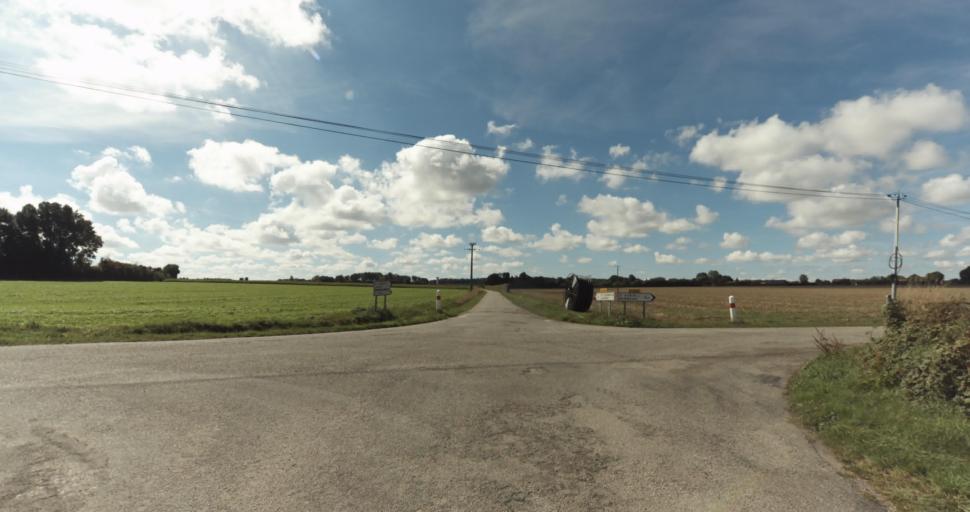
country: FR
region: Lower Normandy
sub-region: Departement du Calvados
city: Orbec
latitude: 48.9415
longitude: 0.3876
